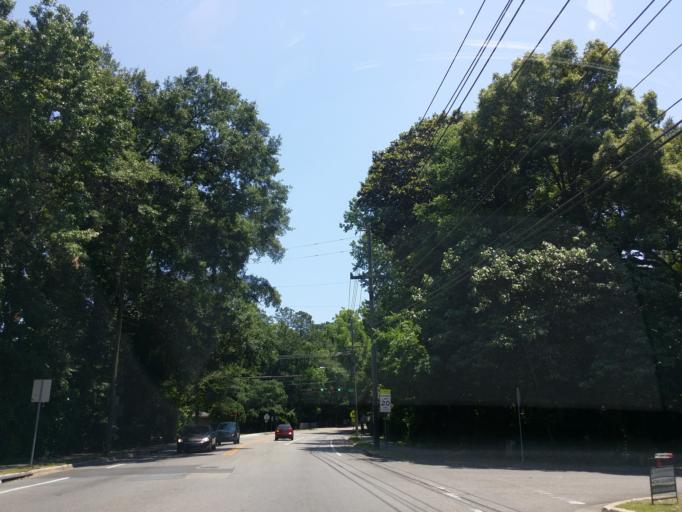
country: US
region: Florida
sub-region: Leon County
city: Tallahassee
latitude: 30.4737
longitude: -84.3238
